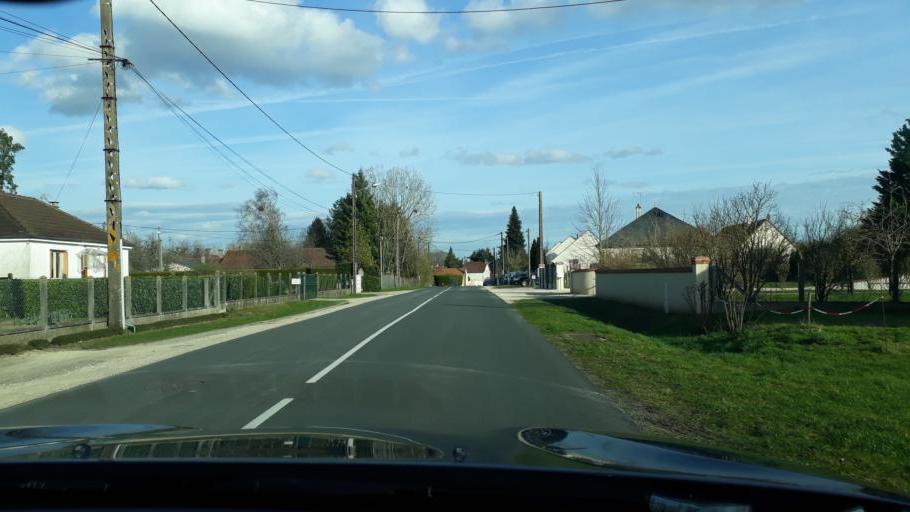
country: FR
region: Centre
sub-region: Departement du Loiret
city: Chilleurs-aux-Bois
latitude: 48.0562
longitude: 2.1902
